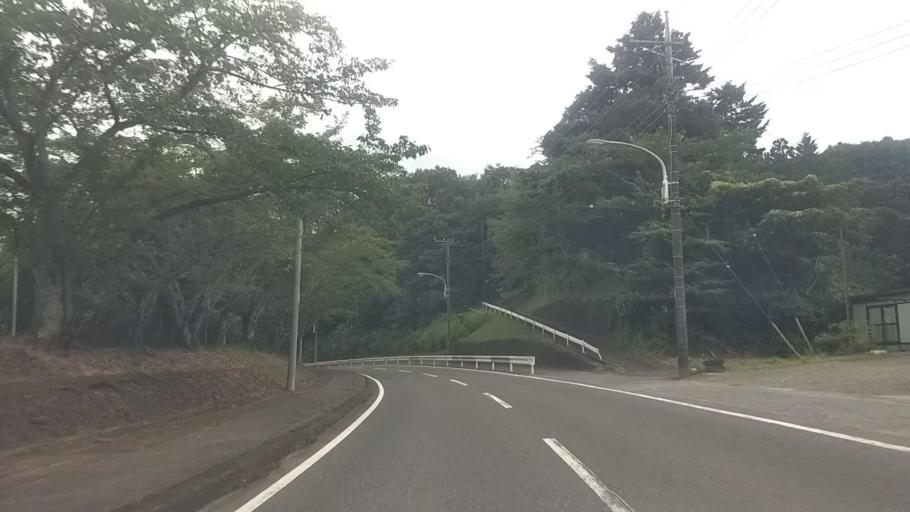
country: JP
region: Chiba
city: Kawaguchi
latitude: 35.2283
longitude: 140.0896
